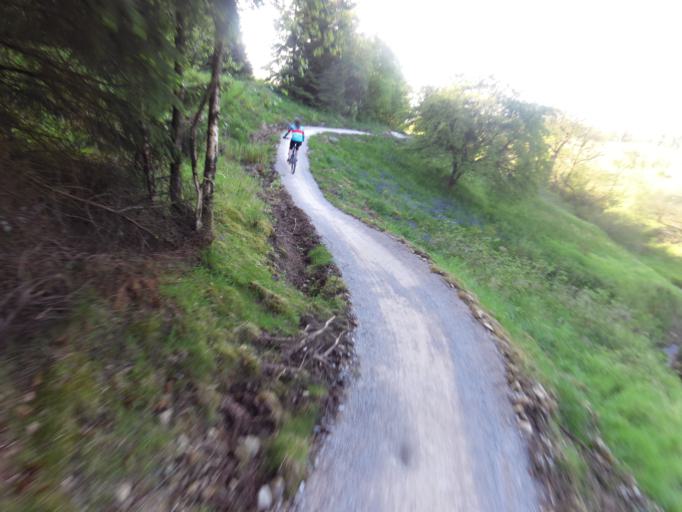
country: GB
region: England
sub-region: North Yorkshire
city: Settle
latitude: 54.0053
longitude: -2.3827
